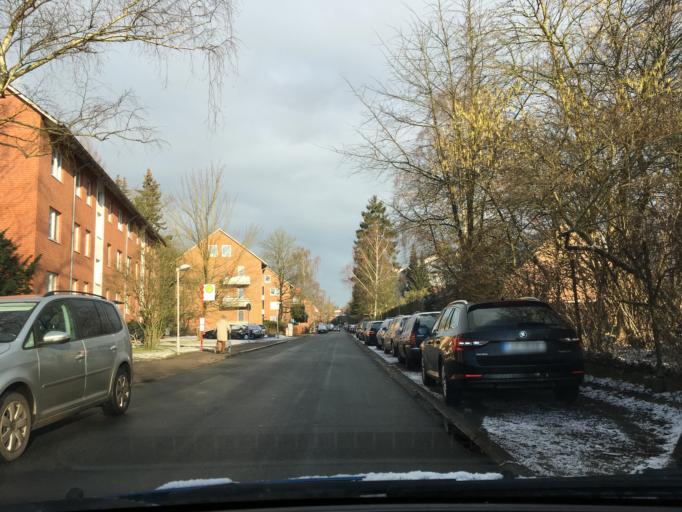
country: DE
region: Lower Saxony
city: Lueneburg
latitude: 53.2266
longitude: 10.3980
